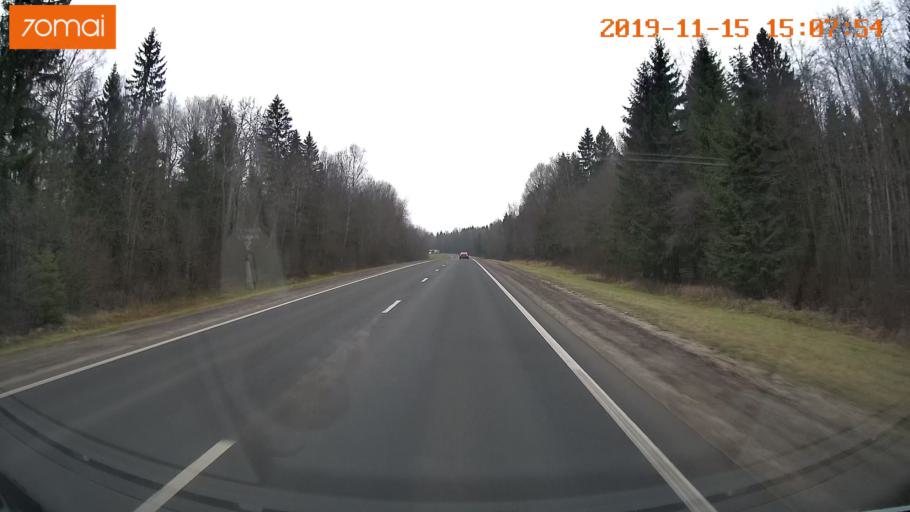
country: RU
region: Jaroslavl
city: Prechistoye
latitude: 58.3779
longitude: 40.2857
